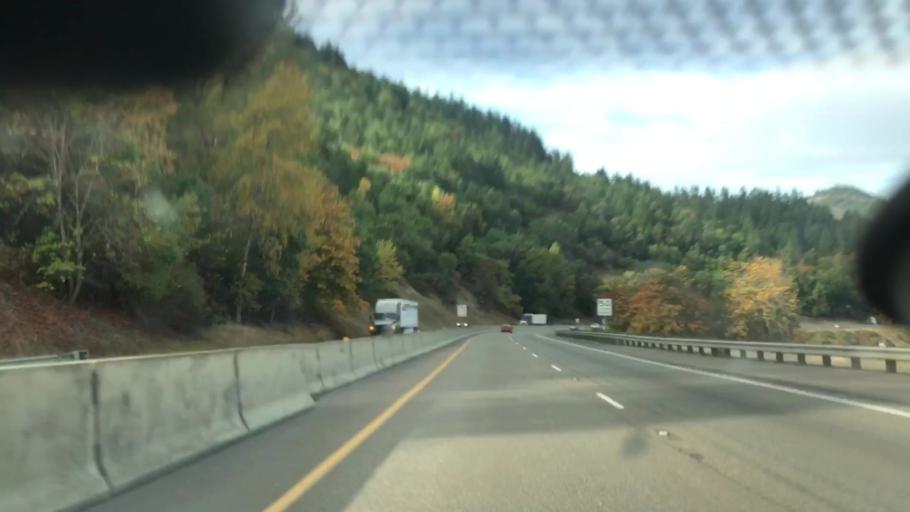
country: US
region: Oregon
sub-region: Douglas County
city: Myrtle Creek
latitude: 43.0165
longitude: -123.3011
